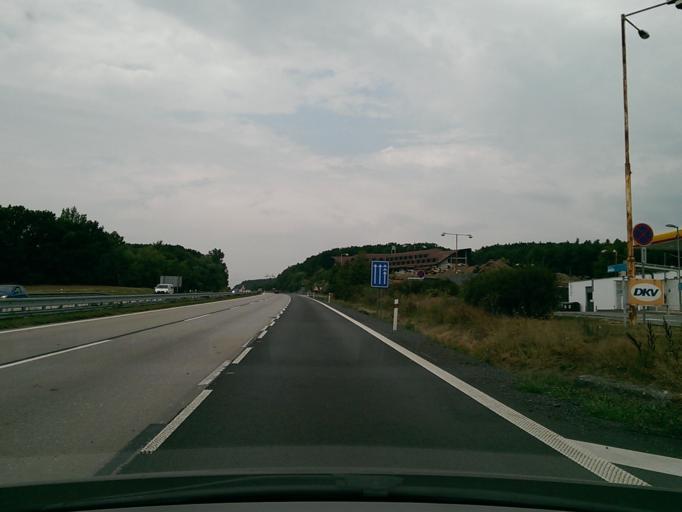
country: CZ
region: South Moravian
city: Troubsko
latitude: 49.1824
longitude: 16.4797
